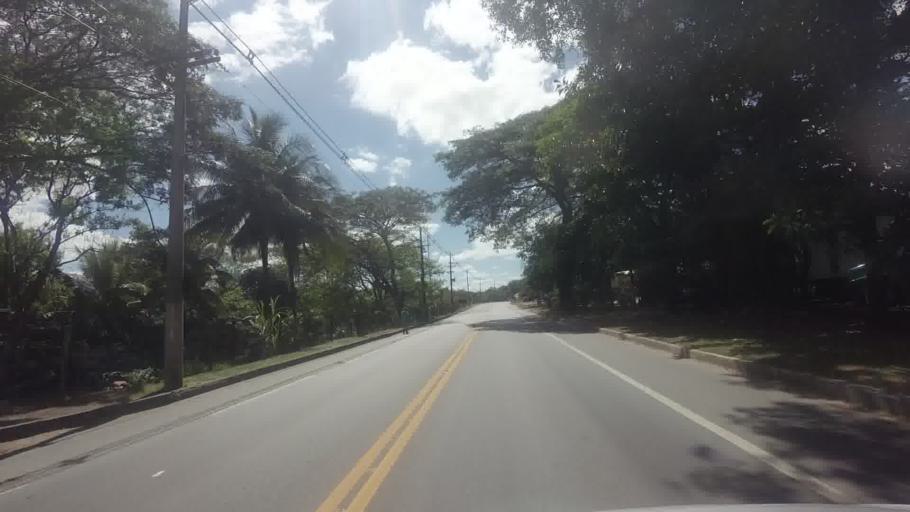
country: BR
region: Minas Gerais
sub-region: Alem Paraiba
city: Alem Paraiba
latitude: -21.8781
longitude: -42.6767
